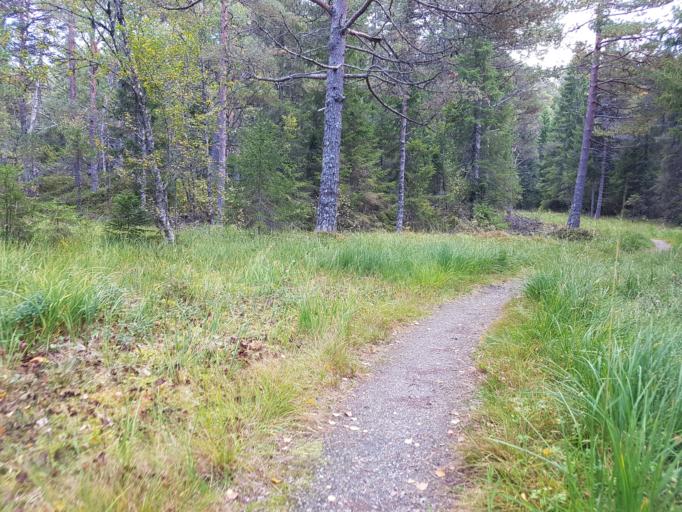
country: NO
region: Sor-Trondelag
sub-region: Trondheim
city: Trondheim
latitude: 63.4363
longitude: 10.2929
